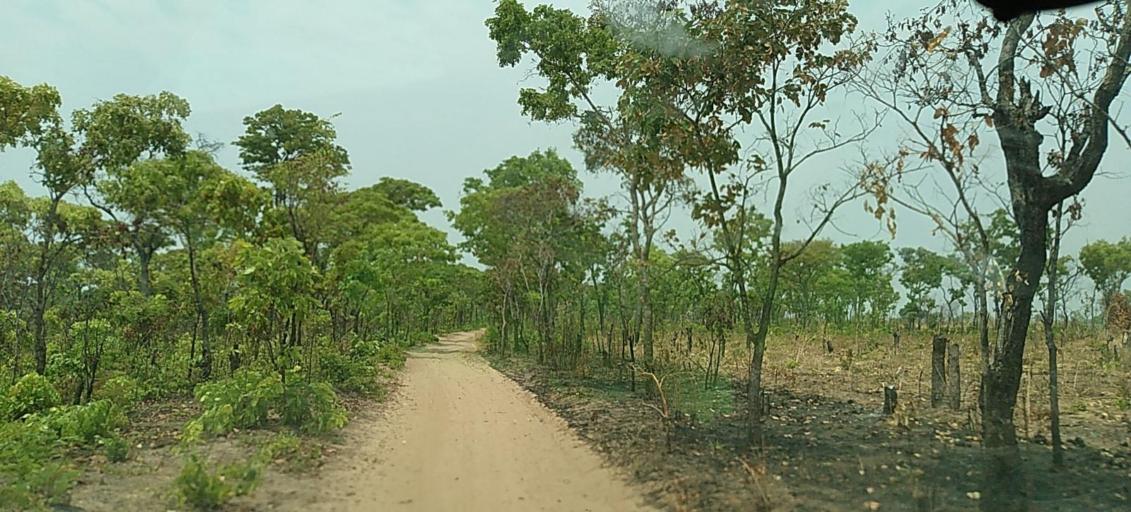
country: ZM
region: North-Western
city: Kabompo
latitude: -13.5262
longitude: 24.4641
